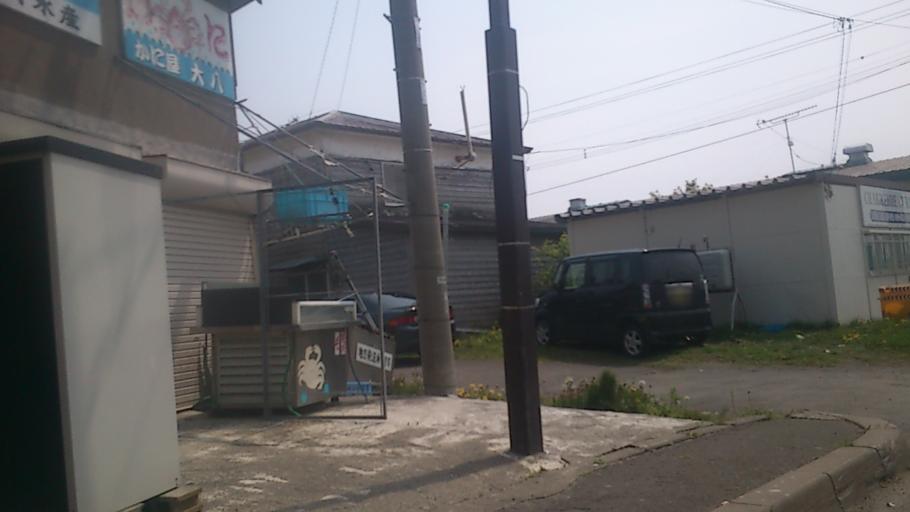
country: JP
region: Hokkaido
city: Nemuro
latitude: 43.2866
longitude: 145.5836
